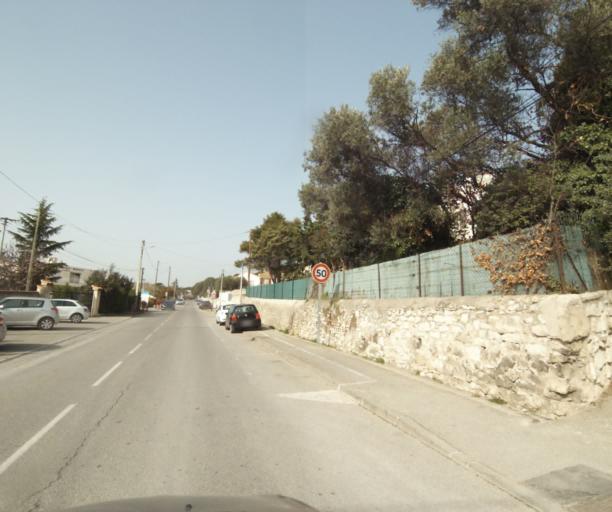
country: FR
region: Provence-Alpes-Cote d'Azur
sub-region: Departement des Bouches-du-Rhone
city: Marseille 15
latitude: 43.3872
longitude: 5.3460
